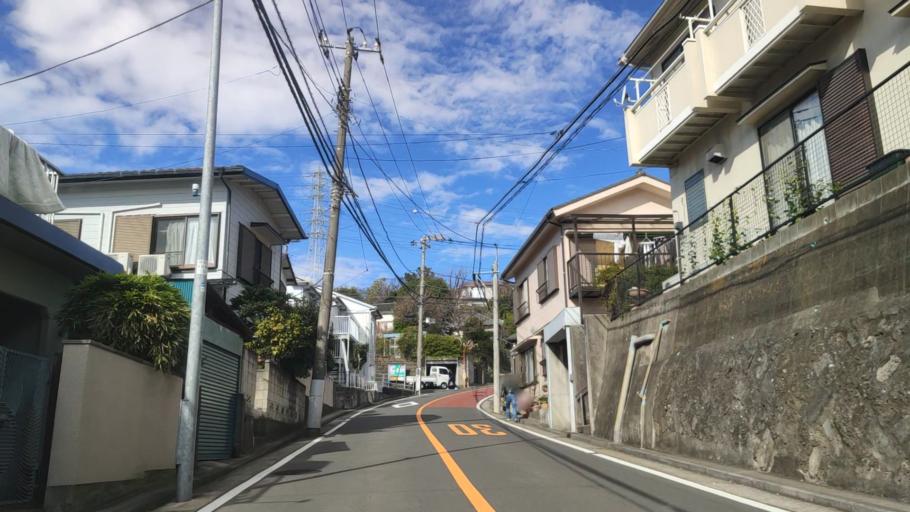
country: JP
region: Kanagawa
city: Yokohama
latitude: 35.4668
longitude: 139.5848
